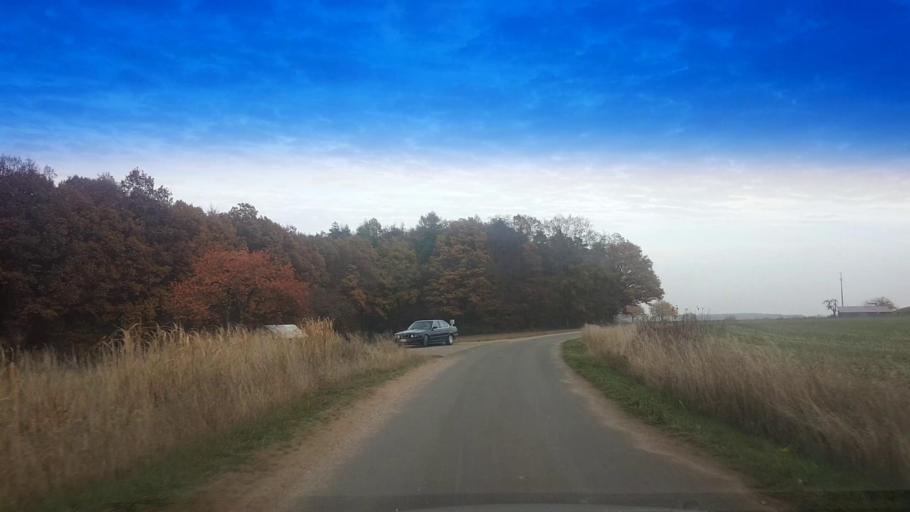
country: DE
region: Bavaria
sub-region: Upper Franconia
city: Priesendorf
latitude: 49.9053
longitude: 10.7466
